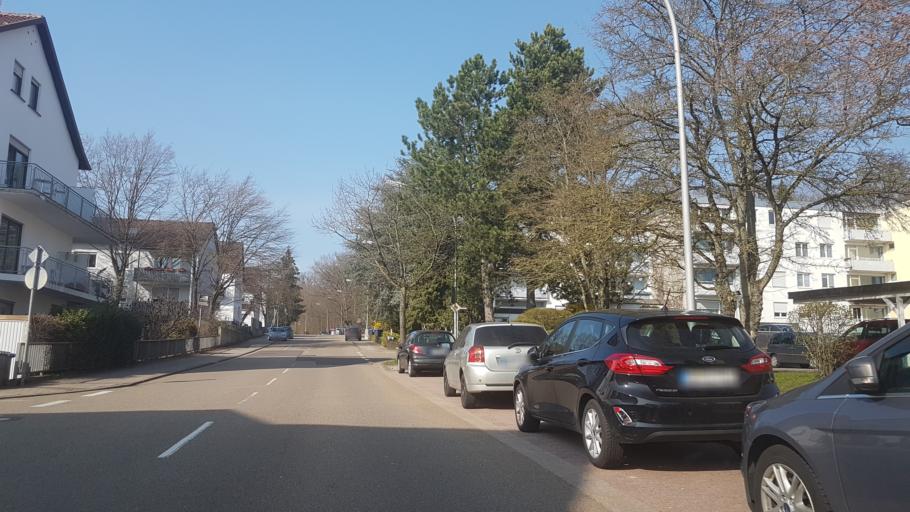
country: DE
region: Saarland
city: Saarbrucken
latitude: 49.2501
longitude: 6.9963
